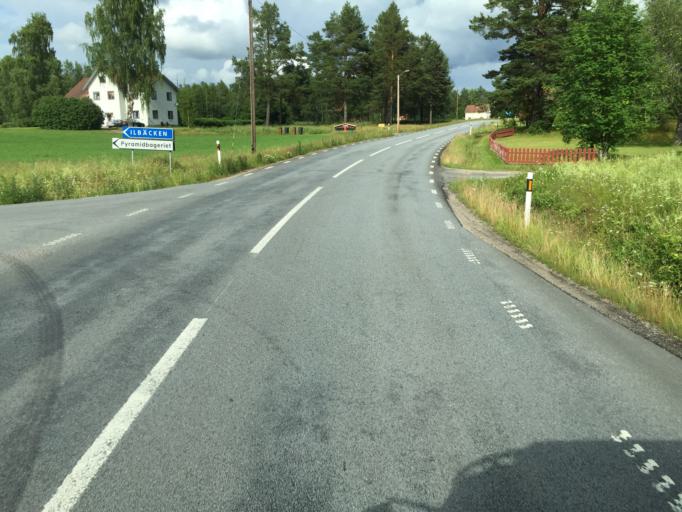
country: SE
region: Dalarna
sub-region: Vansbro Kommun
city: Jarna
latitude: 60.5491
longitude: 14.3091
